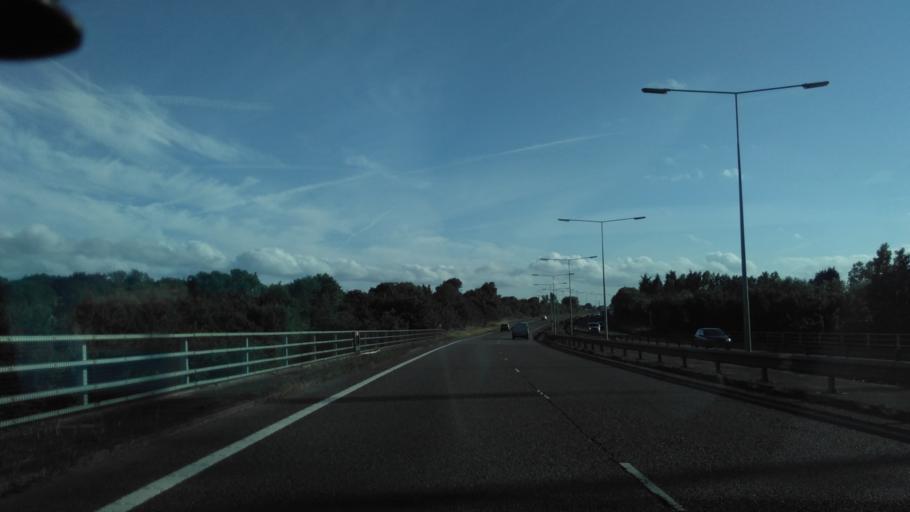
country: GB
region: England
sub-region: Kent
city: Whitstable
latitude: 51.3333
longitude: 1.0009
